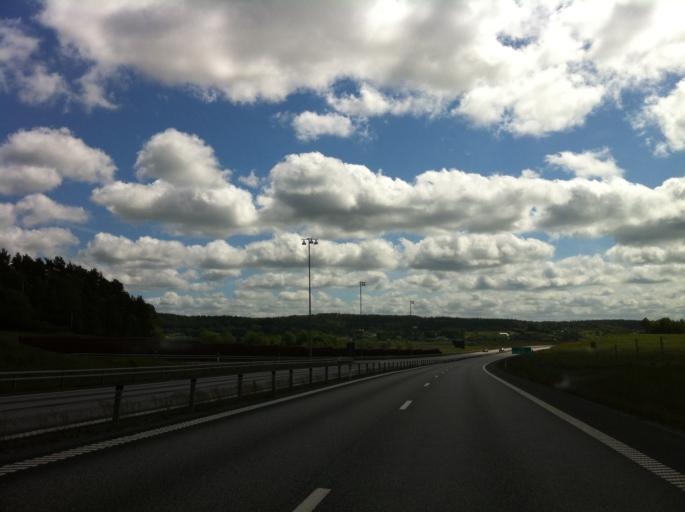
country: SE
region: Vaestra Goetaland
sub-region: Ale Kommun
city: Skepplanda
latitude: 57.9858
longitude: 12.1625
